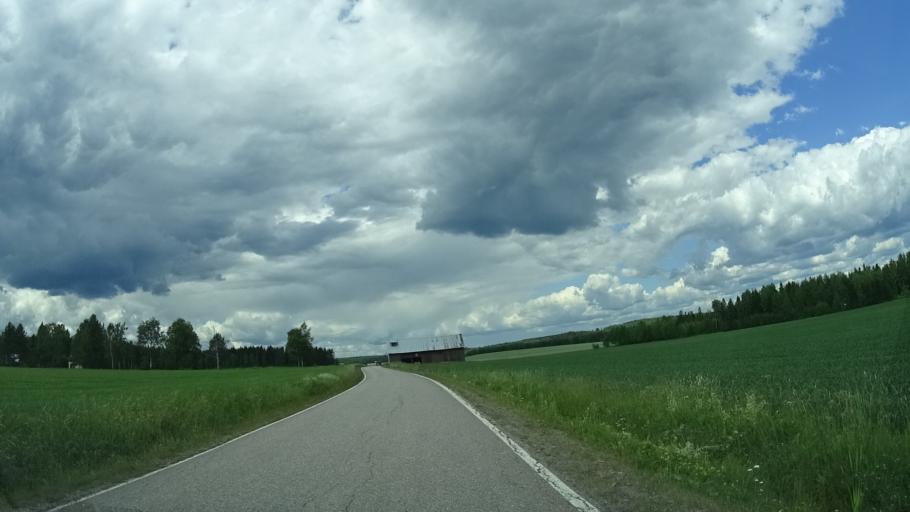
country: FI
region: Uusimaa
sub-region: Helsinki
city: Espoo
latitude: 60.4132
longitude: 24.5560
